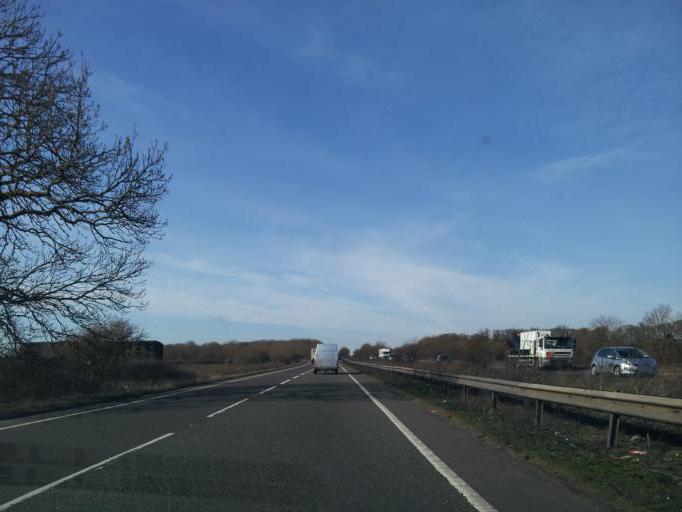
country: GB
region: England
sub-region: District of Rutland
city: Tickencote
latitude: 52.6873
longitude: -0.5551
